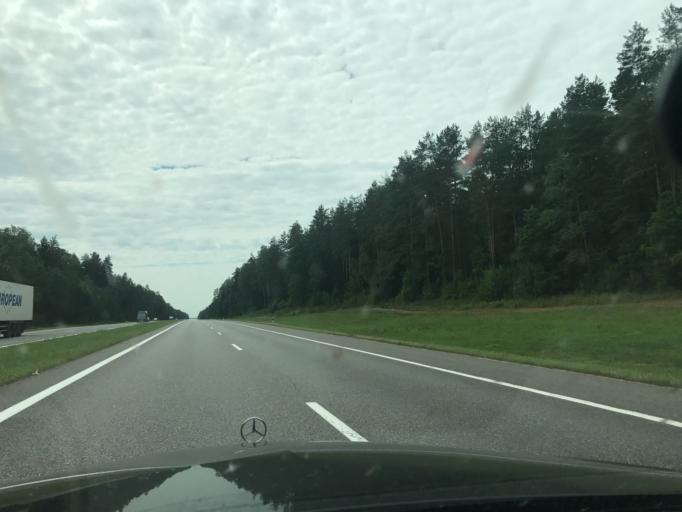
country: BY
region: Minsk
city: Slabada
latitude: 53.9252
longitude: 27.9572
